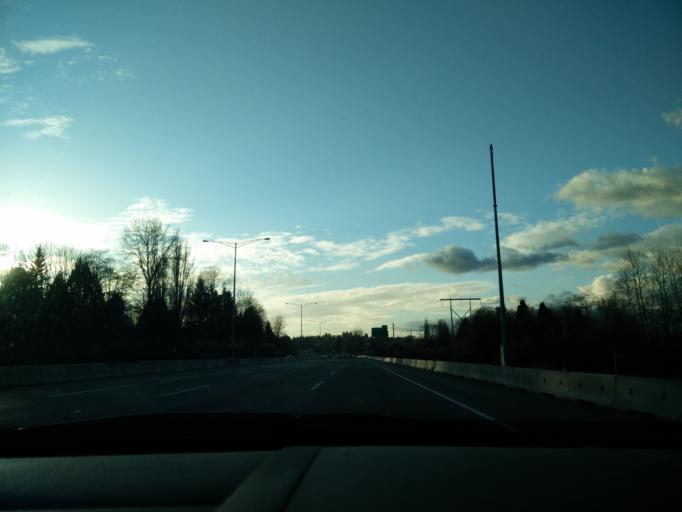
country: CA
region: British Columbia
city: Burnaby
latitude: 49.2392
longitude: -122.9519
